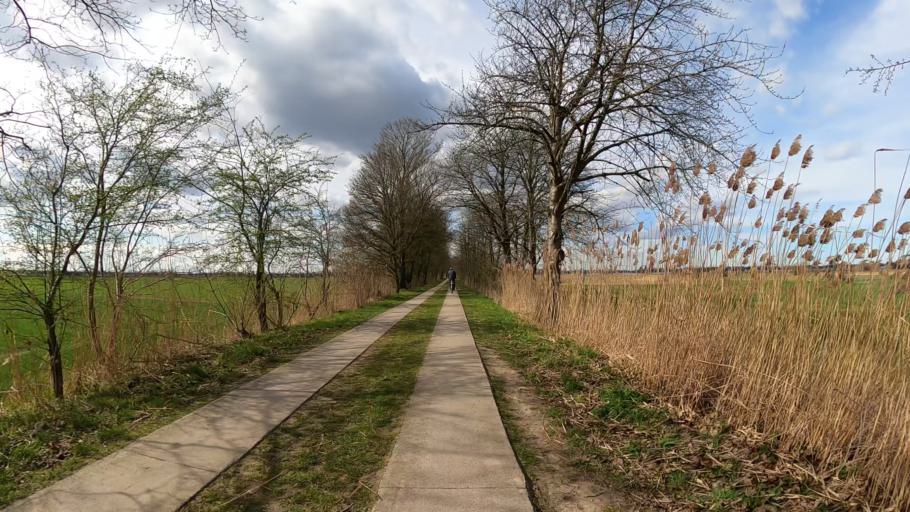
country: DE
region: Lower Saxony
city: Stelle
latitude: 53.4657
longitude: 10.0981
